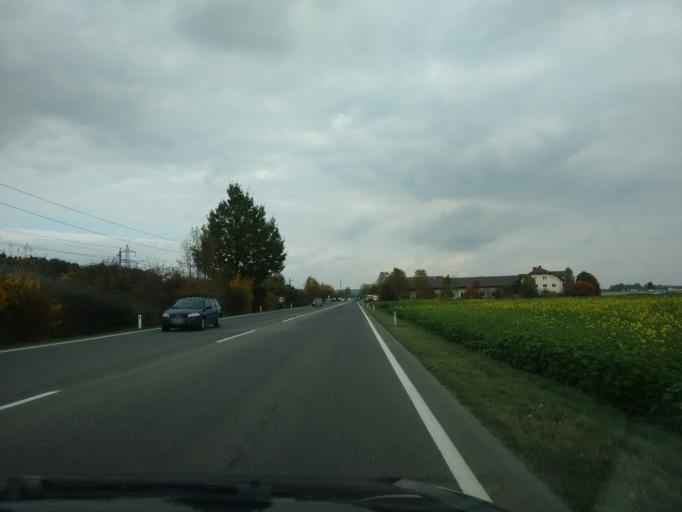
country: AT
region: Upper Austria
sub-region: Politischer Bezirk Vocklabruck
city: Redlham
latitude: 48.0308
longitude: 13.7384
